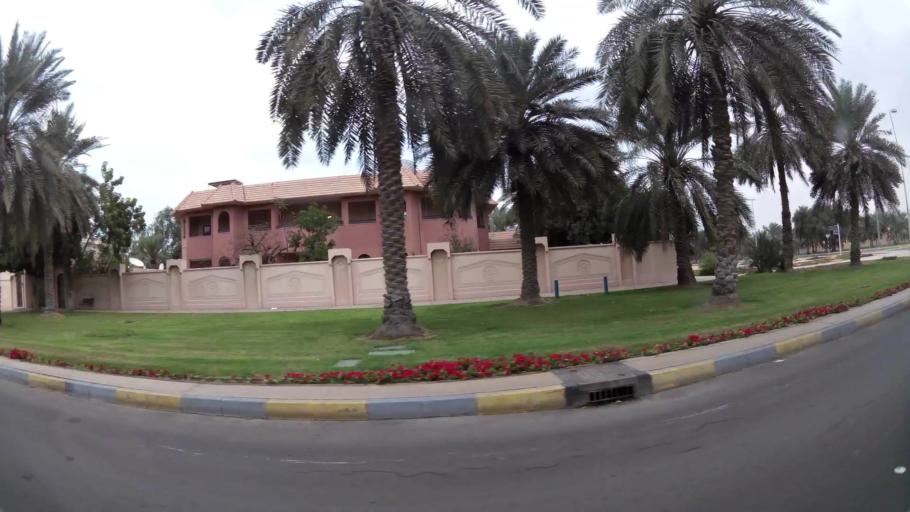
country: AE
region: Abu Dhabi
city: Abu Dhabi
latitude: 24.4415
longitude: 54.3606
